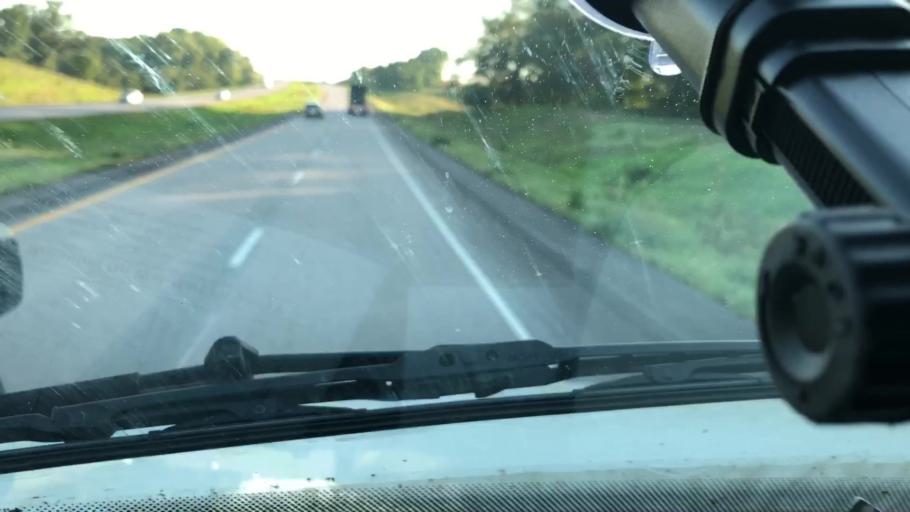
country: US
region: Iowa
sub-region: Pottawattamie County
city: Council Bluffs
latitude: 41.3307
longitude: -95.7430
